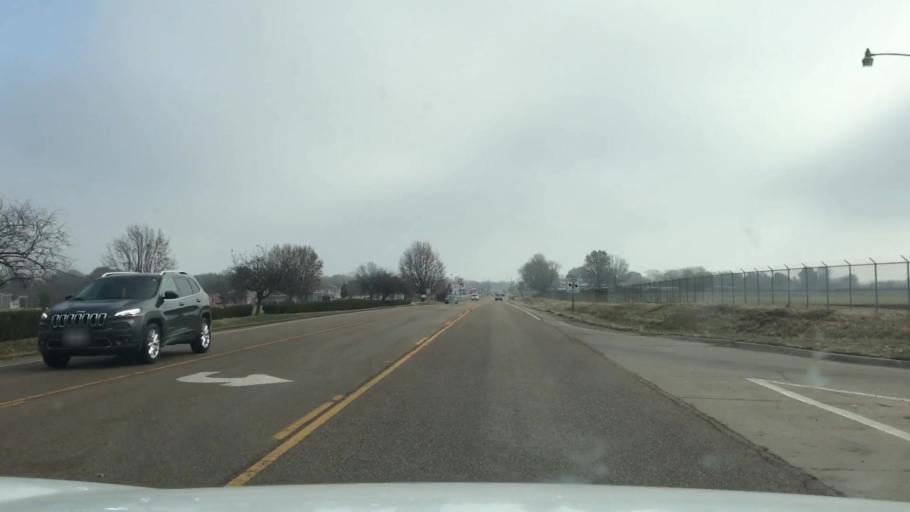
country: US
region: Illinois
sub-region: Madison County
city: Bethalto
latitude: 38.9007
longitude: -90.0550
